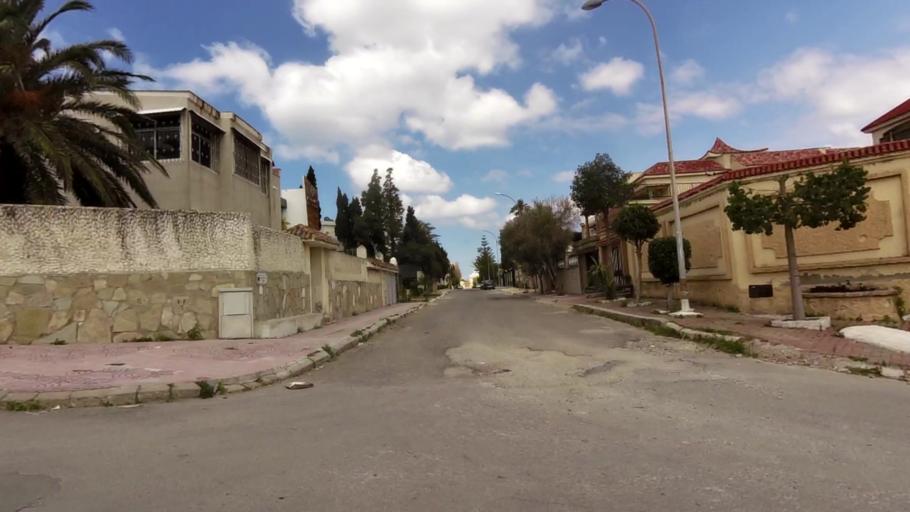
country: MA
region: Tanger-Tetouan
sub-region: Tanger-Assilah
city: Tangier
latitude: 35.7731
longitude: -5.7722
